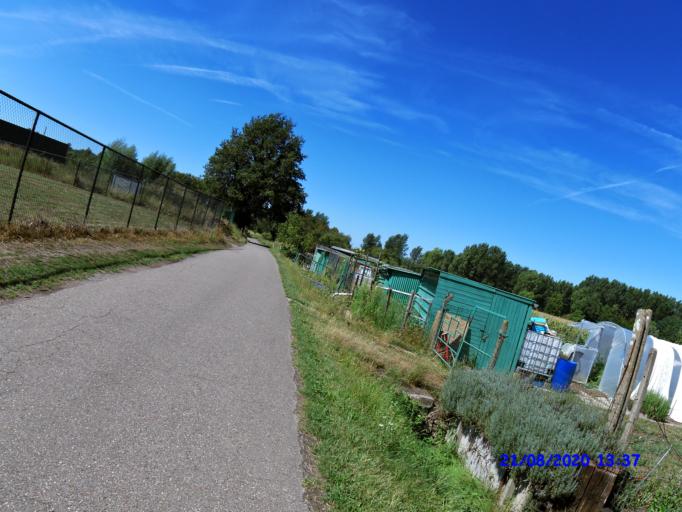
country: BE
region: Flanders
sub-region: Provincie Limburg
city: Sint-Truiden
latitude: 50.8178
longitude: 5.1709
